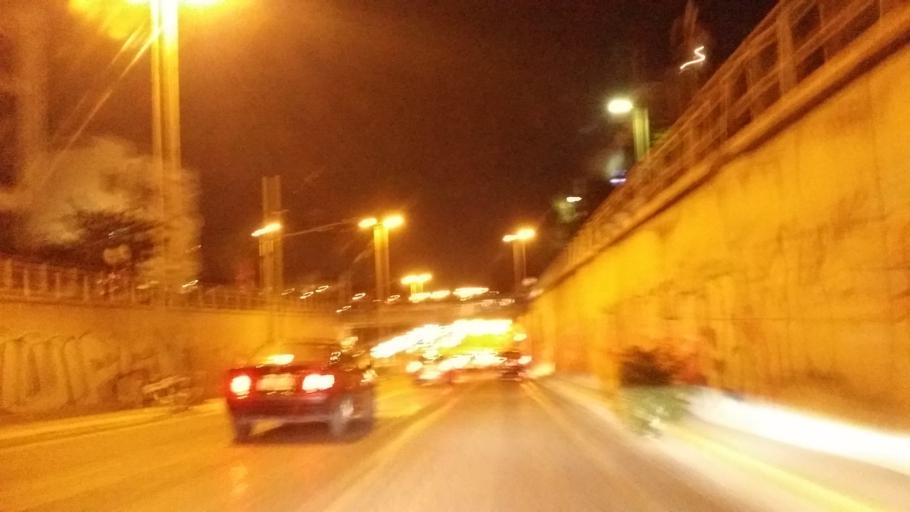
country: GR
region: Attica
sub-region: Nomarchia Athinas
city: Filothei
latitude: 38.0232
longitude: 23.7907
